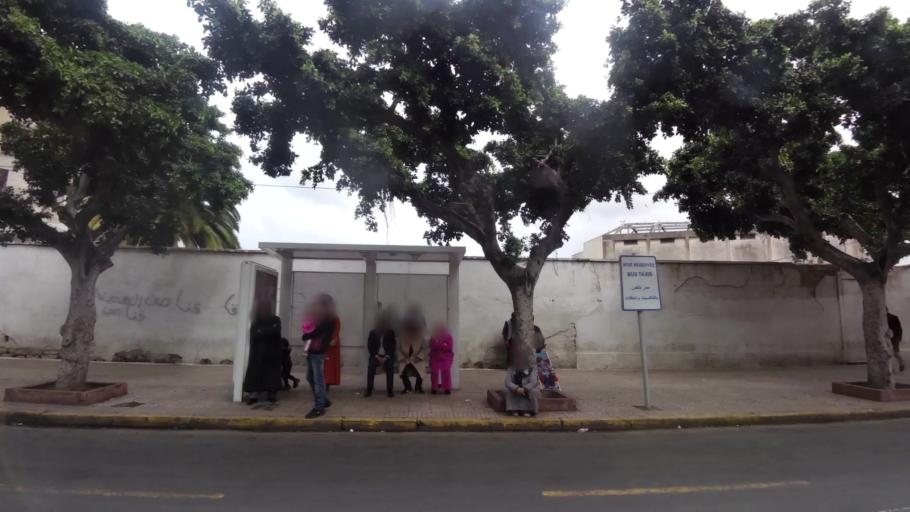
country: MA
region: Grand Casablanca
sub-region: Casablanca
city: Casablanca
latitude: 33.5945
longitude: -7.6225
